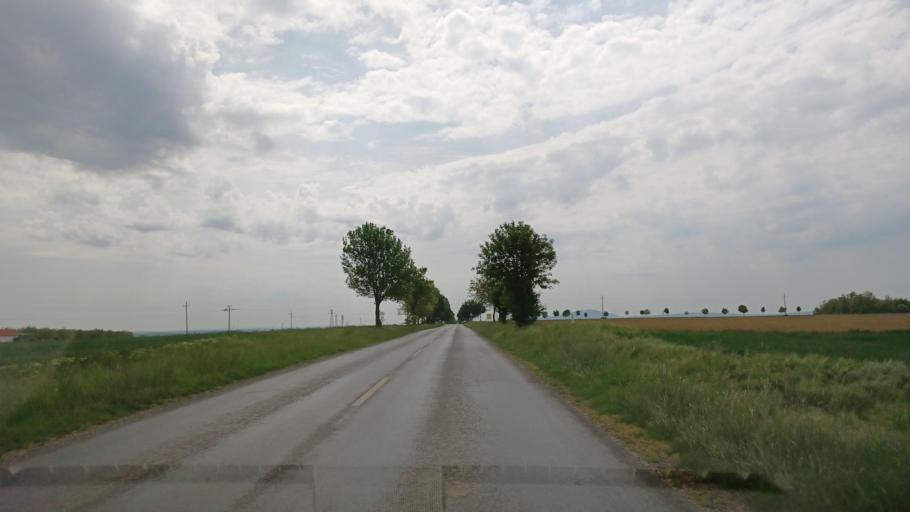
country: HU
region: Baranya
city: Kozarmisleny
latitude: 46.0012
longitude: 18.3160
